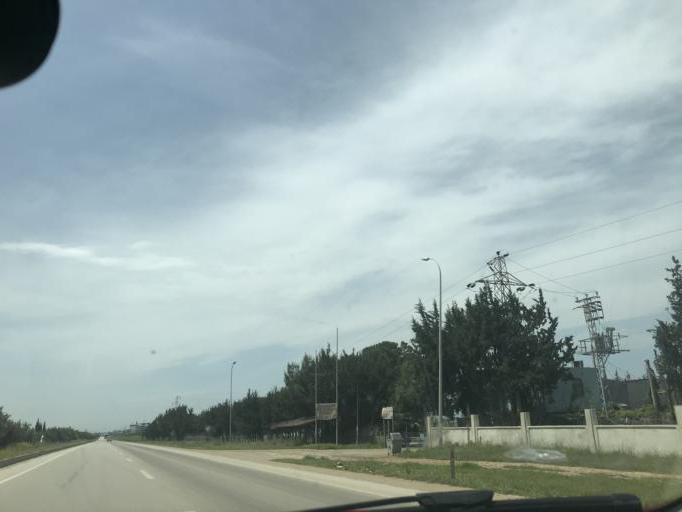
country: TR
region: Adana
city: Yuregir
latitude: 36.9756
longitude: 35.4878
